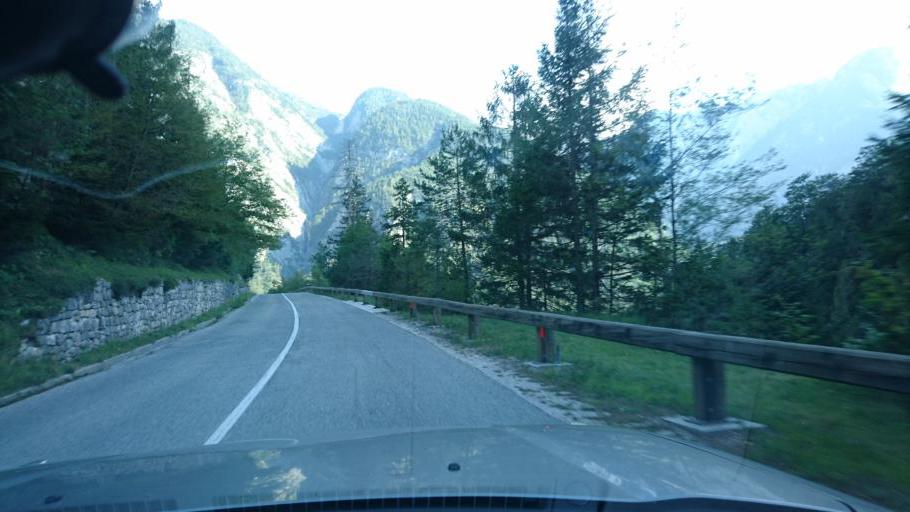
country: SI
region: Kranjska Gora
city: Kranjska Gora
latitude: 46.3864
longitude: 13.7505
